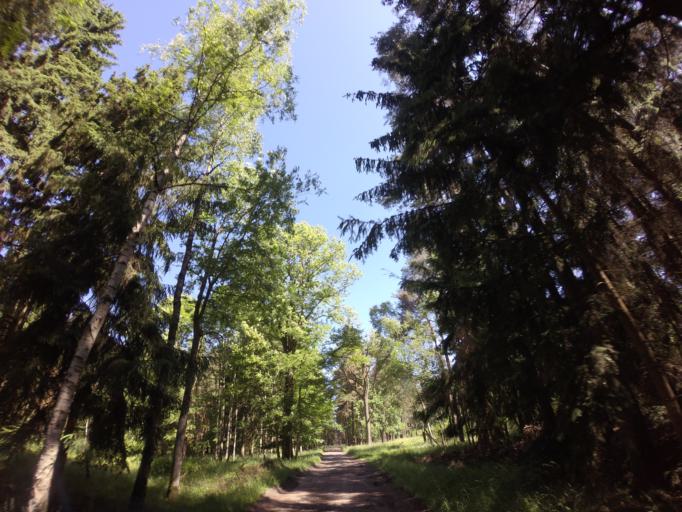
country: PL
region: West Pomeranian Voivodeship
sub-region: Powiat walecki
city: Czlopa
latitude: 53.1446
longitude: 15.9689
